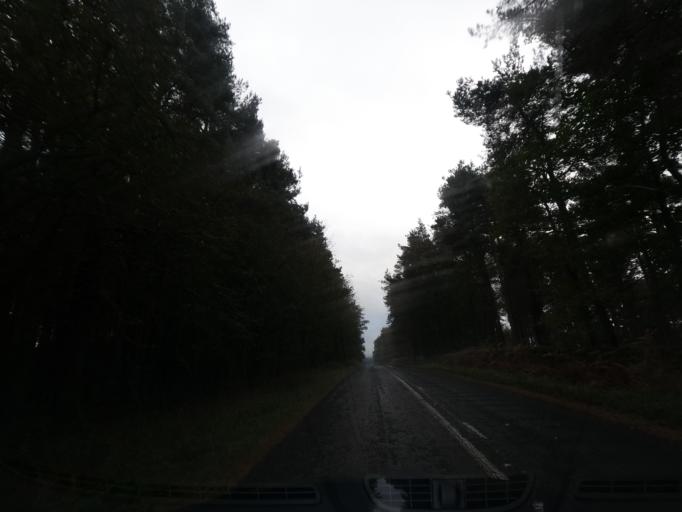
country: GB
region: England
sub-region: Northumberland
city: Doddington
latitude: 55.6027
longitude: -2.0016
